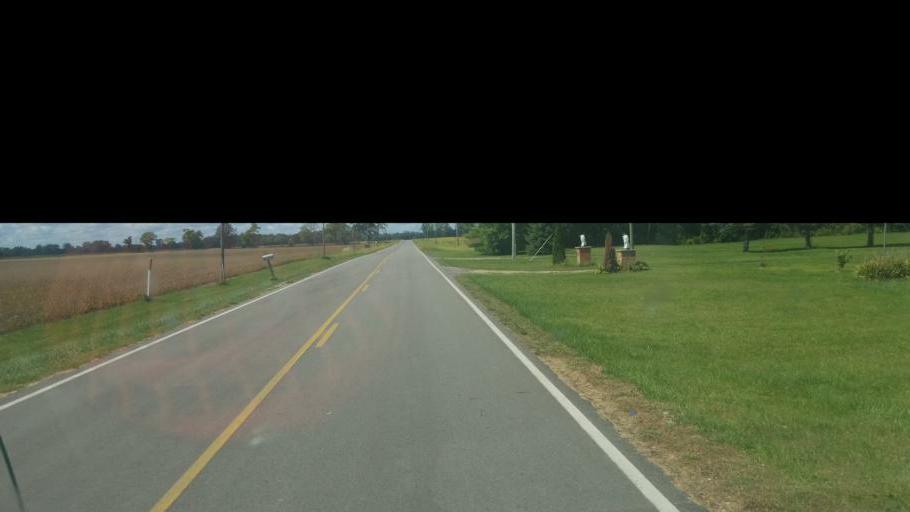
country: US
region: Ohio
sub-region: Champaign County
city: North Lewisburg
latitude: 40.2015
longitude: -83.4833
